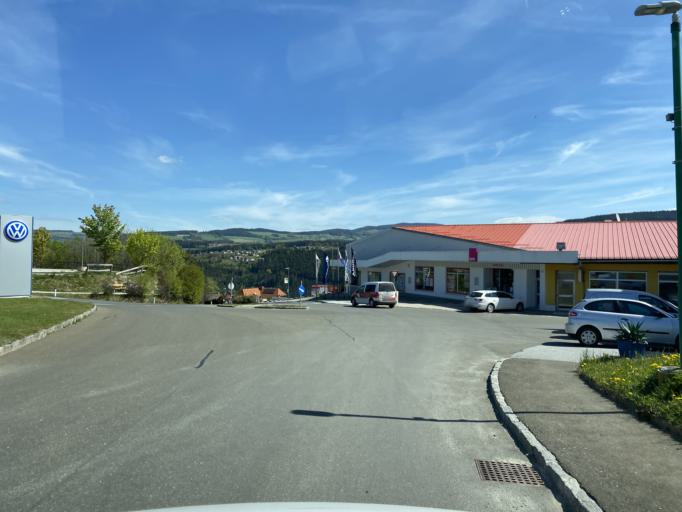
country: AT
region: Styria
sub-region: Politischer Bezirk Weiz
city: Birkfeld
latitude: 47.3478
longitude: 15.6915
